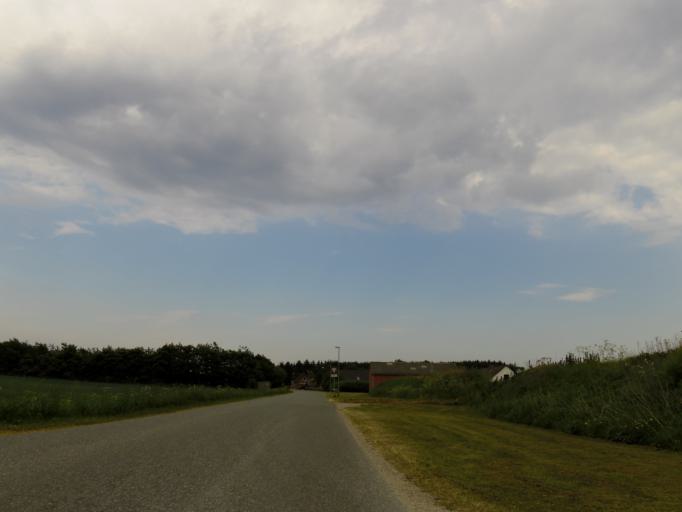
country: DK
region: Central Jutland
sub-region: Holstebro Kommune
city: Vinderup
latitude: 56.4966
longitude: 8.7869
